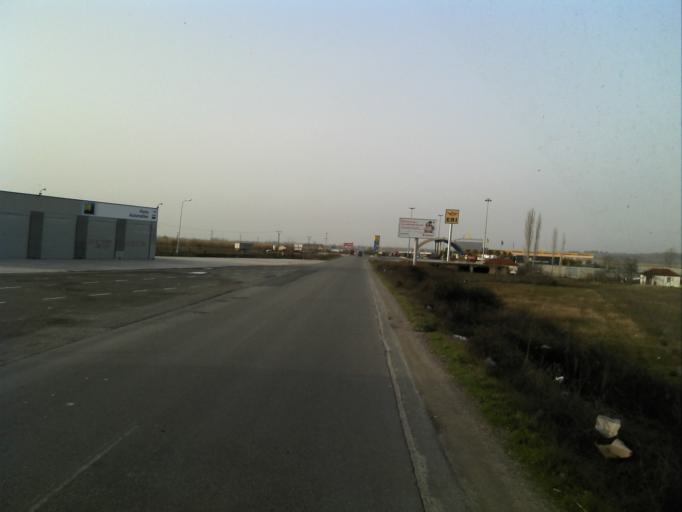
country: AL
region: Durres
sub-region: Rrethi i Krujes
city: Thumane
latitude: 41.5167
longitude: 19.6893
